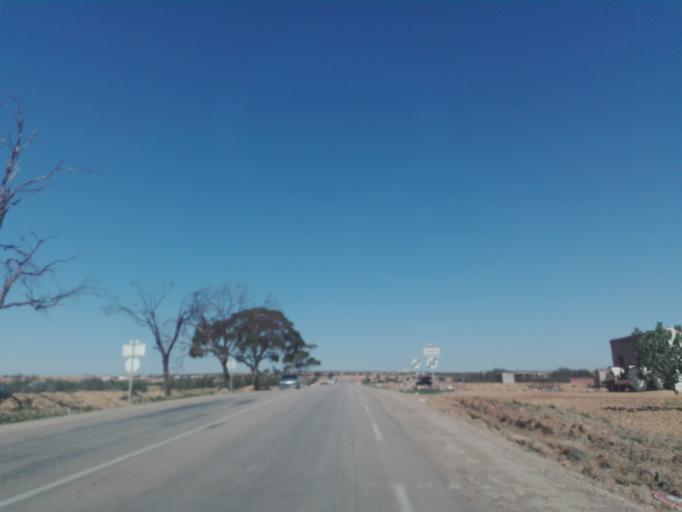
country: TN
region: Safaqis
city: Bi'r `Ali Bin Khalifah
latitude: 34.7429
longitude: 10.3671
